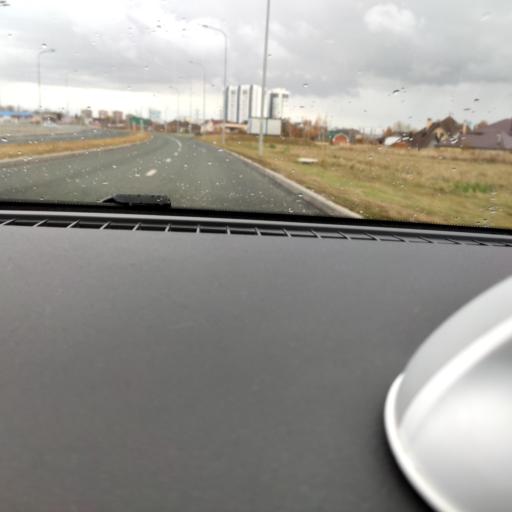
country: RU
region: Samara
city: Samara
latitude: 53.2748
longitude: 50.2321
